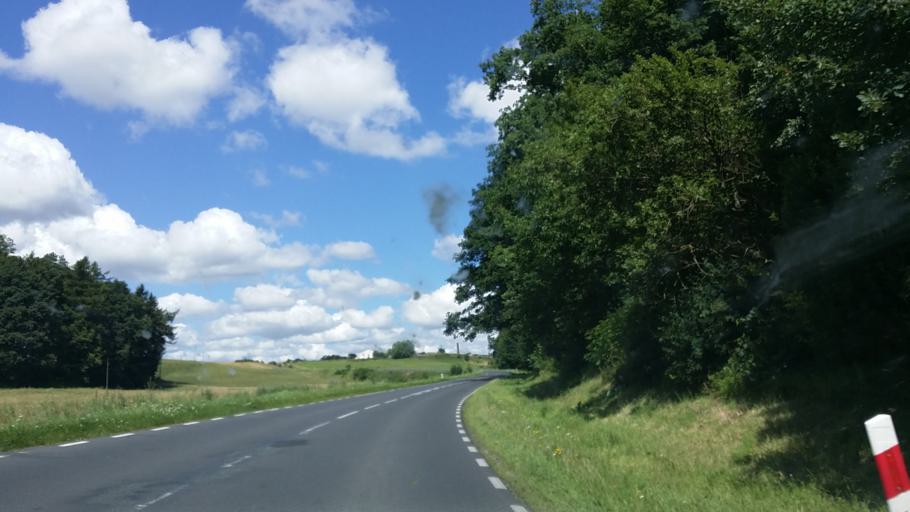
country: PL
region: West Pomeranian Voivodeship
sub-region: Powiat swidwinski
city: Swidwin
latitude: 53.8050
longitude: 15.7708
